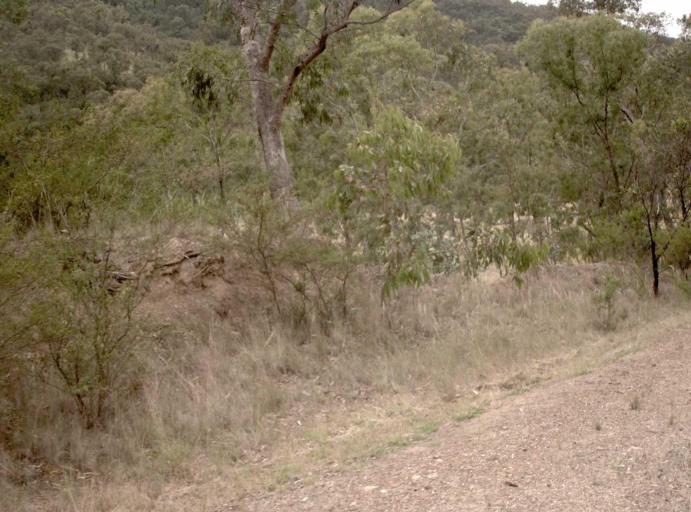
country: AU
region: Victoria
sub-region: East Gippsland
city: Bairnsdale
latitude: -37.5337
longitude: 147.2145
